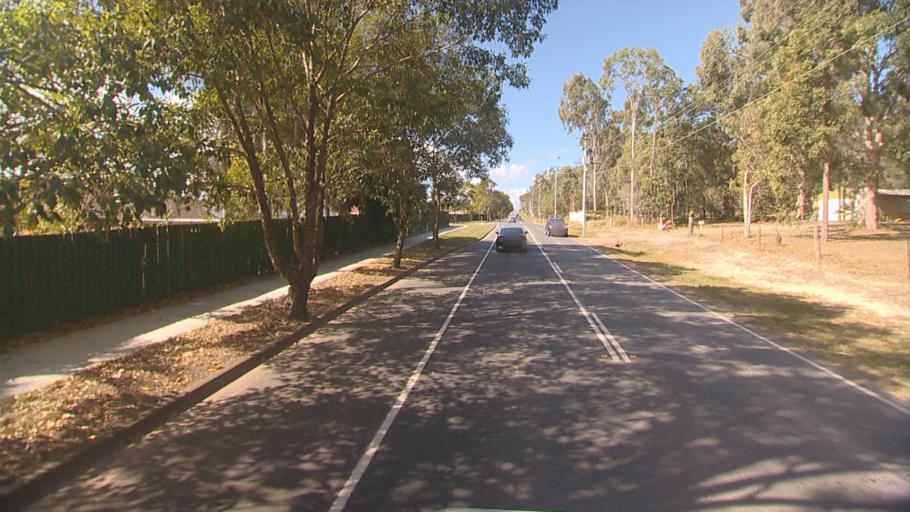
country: AU
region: Queensland
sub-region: Logan
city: Park Ridge South
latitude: -27.6876
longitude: 153.0389
